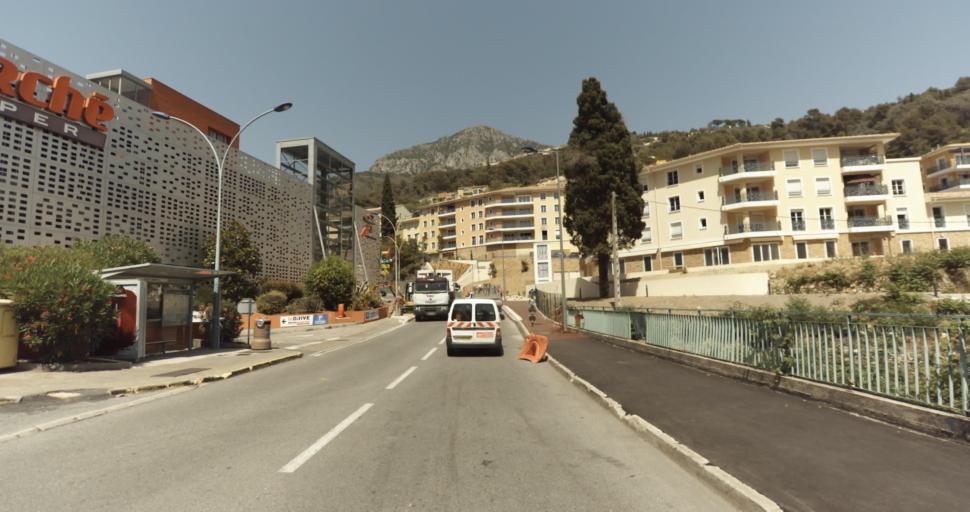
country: FR
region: Provence-Alpes-Cote d'Azur
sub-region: Departement des Alpes-Maritimes
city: Sainte-Agnes
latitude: 43.7995
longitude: 7.4879
